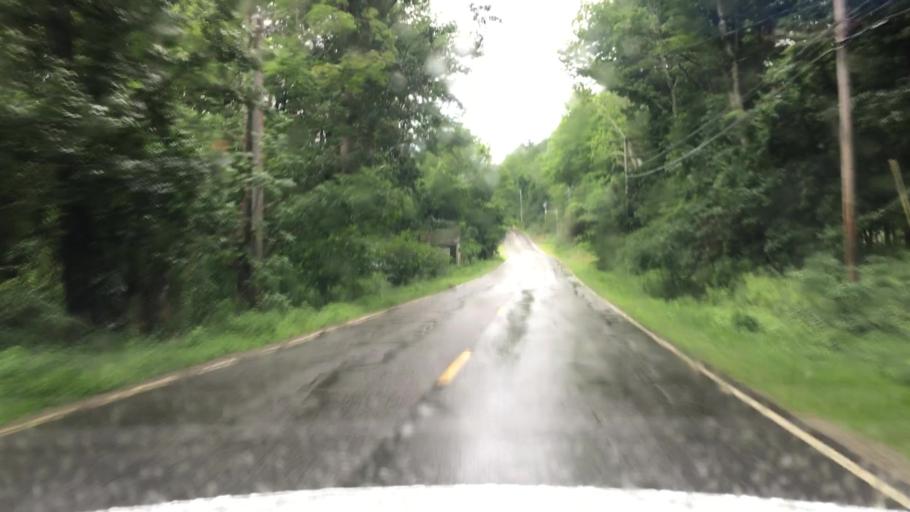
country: US
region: Maine
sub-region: Kennebec County
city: Winthrop
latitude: 44.3014
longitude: -69.9242
